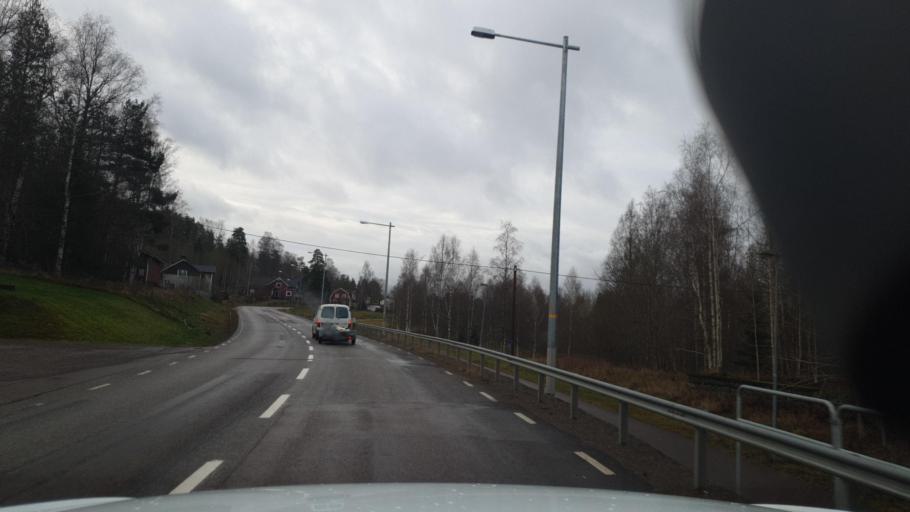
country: SE
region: Vaermland
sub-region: Eda Kommun
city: Amotfors
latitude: 59.7114
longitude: 12.1538
